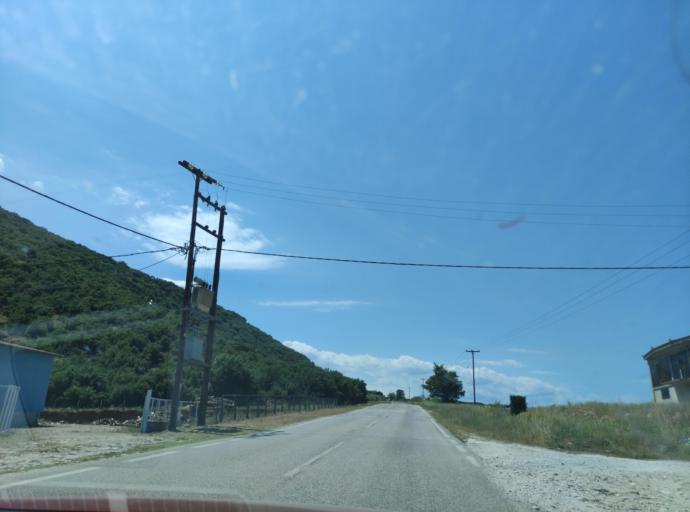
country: GR
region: East Macedonia and Thrace
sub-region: Nomos Kavalas
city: Palaiochori
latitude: 40.9713
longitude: 24.1654
